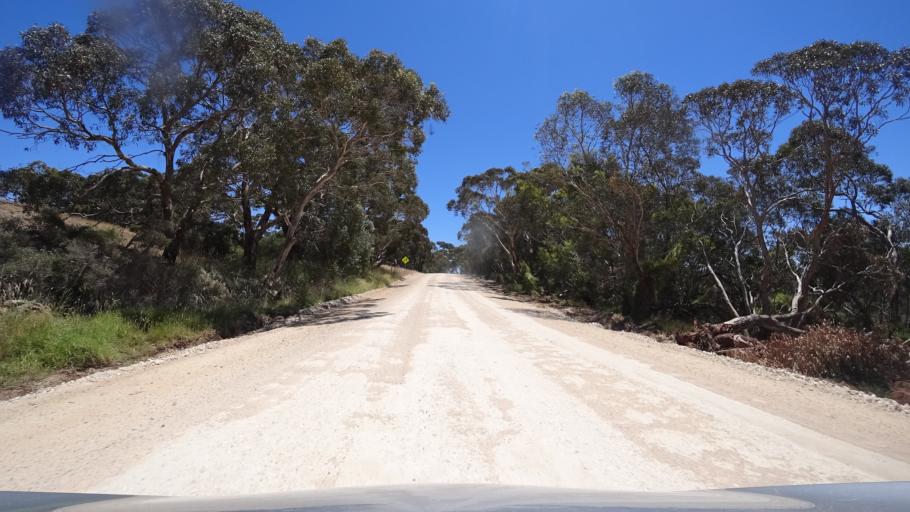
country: AU
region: South Australia
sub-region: Kangaroo Island
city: Kingscote
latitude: -35.6510
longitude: 137.1684
